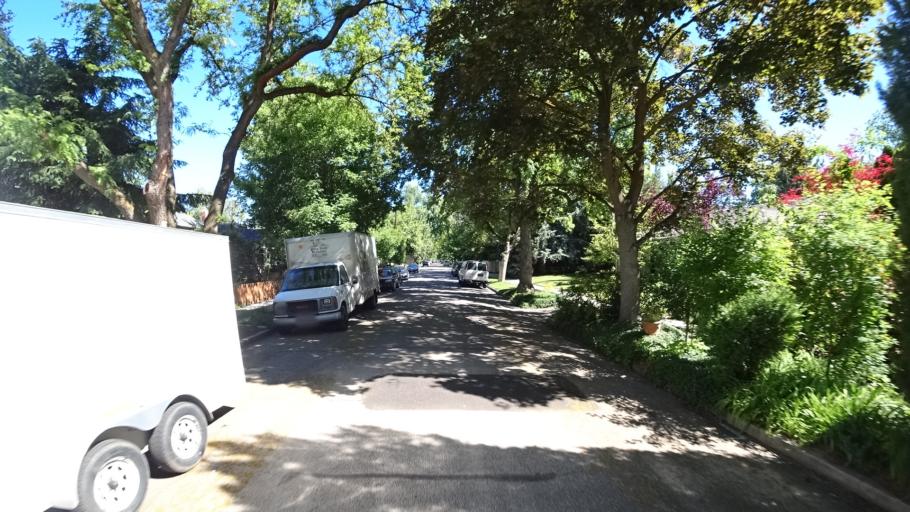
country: US
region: Idaho
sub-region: Ada County
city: Boise
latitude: 43.6277
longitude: -116.2134
